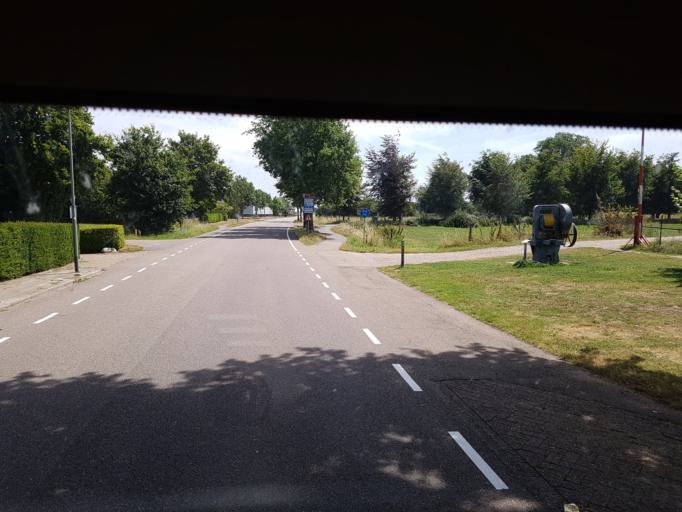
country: NL
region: Limburg
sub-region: Gemeente Maasgouw
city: Maasbracht
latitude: 51.1614
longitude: 5.8478
